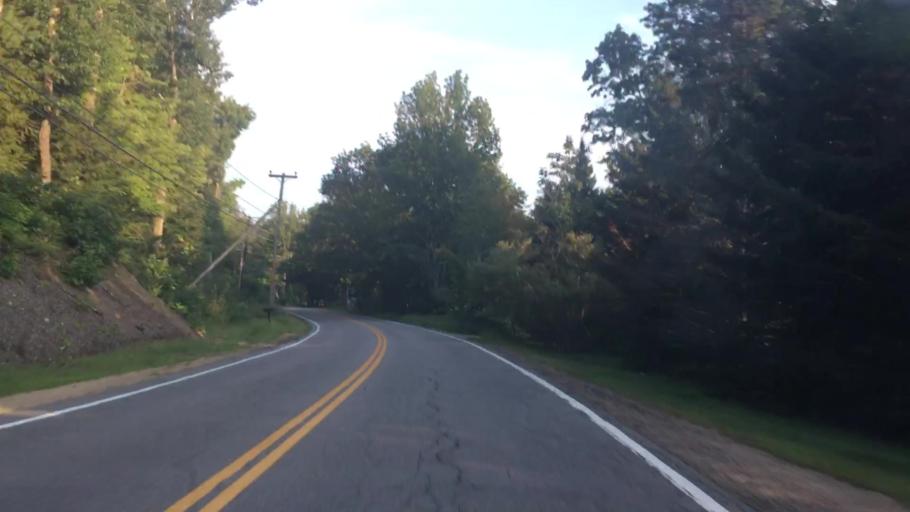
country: US
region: New Hampshire
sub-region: Belknap County
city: Gilmanton
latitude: 43.4716
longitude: -71.4278
